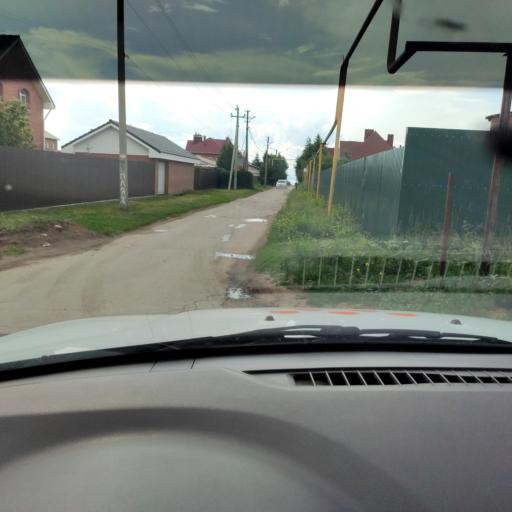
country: RU
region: Samara
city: Podstepki
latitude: 53.6101
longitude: 49.0340
